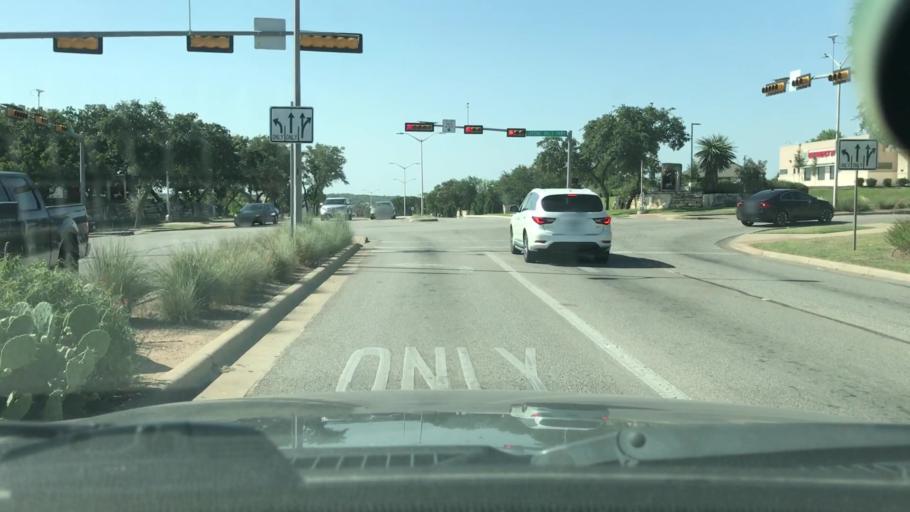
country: US
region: Texas
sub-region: Williamson County
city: Leander
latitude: 30.5451
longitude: -97.8644
